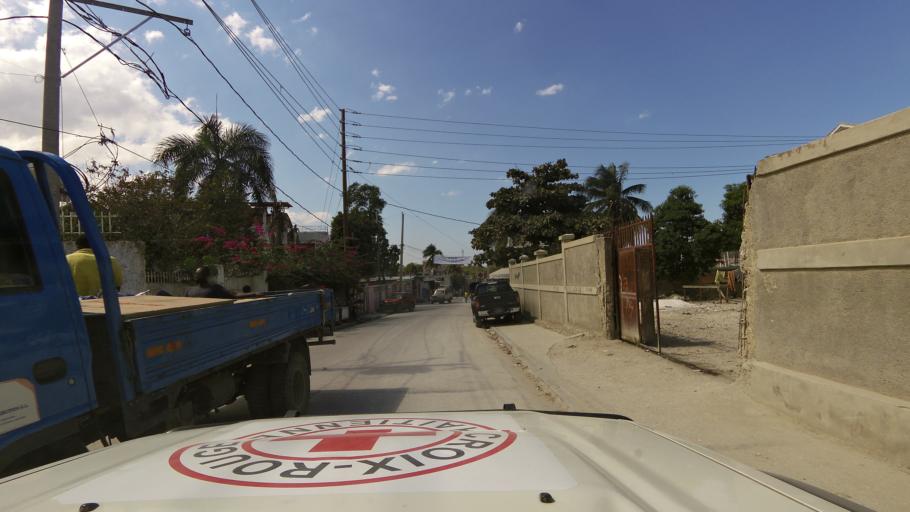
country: HT
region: Ouest
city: Delmas 73
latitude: 18.5516
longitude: -72.2974
